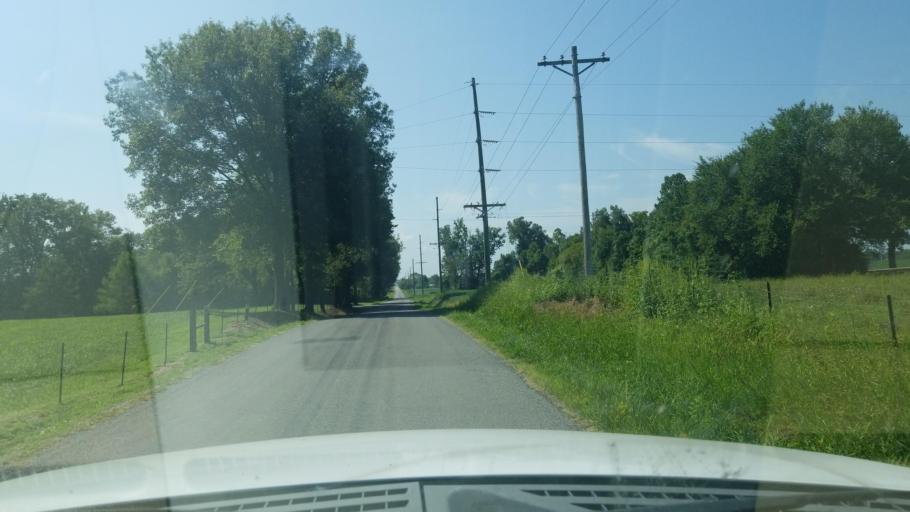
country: US
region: Illinois
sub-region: Saline County
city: Harrisburg
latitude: 37.8500
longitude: -88.6517
